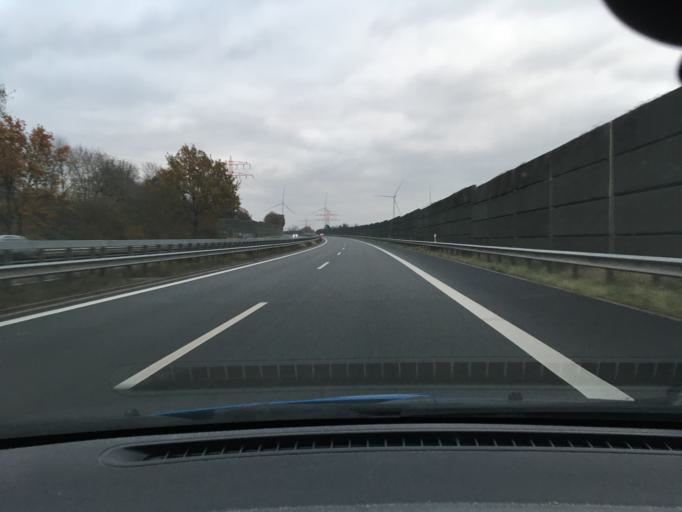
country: DE
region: Hamburg
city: Bergedorf
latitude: 53.4725
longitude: 10.1866
